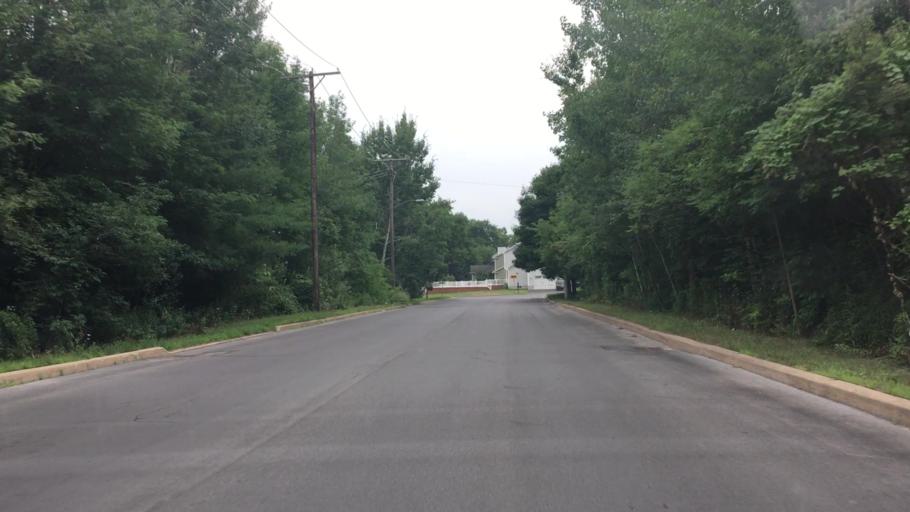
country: US
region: New York
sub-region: Clinton County
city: Plattsburgh West
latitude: 44.6933
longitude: -73.4826
